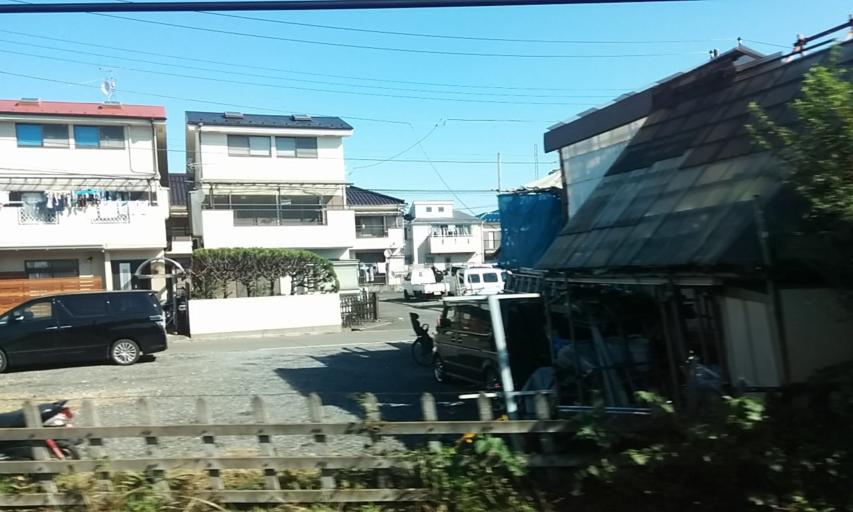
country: JP
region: Tokyo
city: Higashimurayama-shi
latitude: 35.7341
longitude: 139.4949
